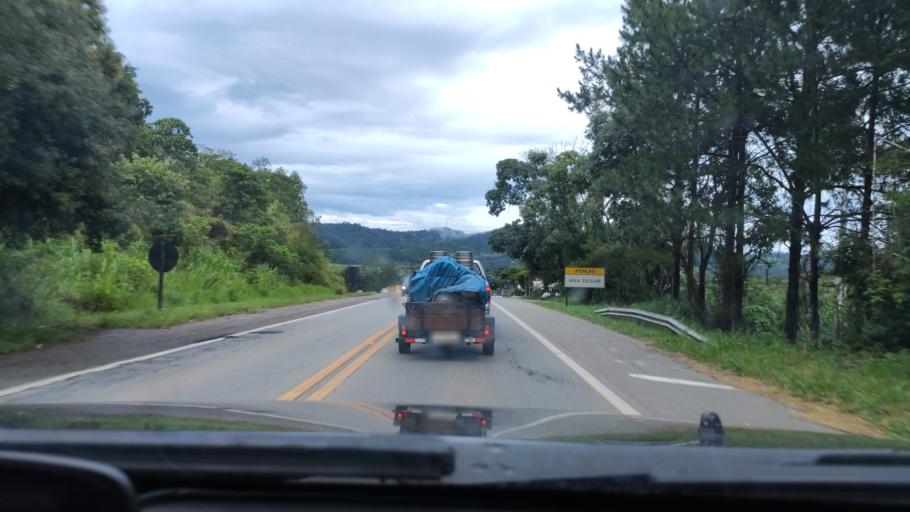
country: BR
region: Sao Paulo
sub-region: Braganca Paulista
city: Braganca Paulista
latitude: -22.8478
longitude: -46.5457
